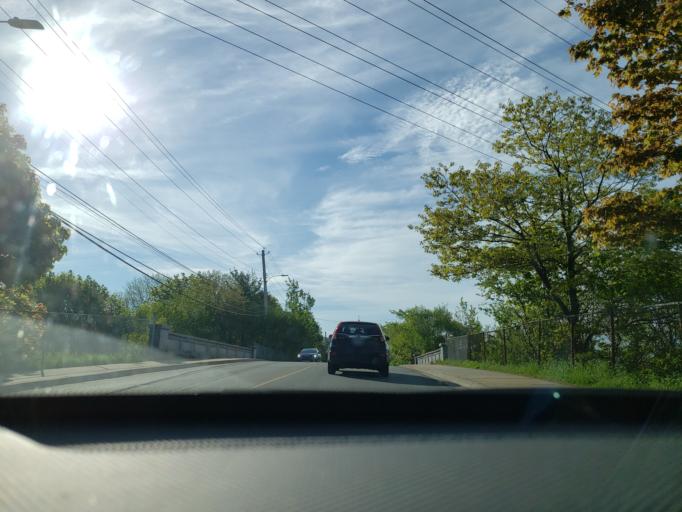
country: CA
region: Nova Scotia
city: Halifax
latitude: 44.6493
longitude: -63.6236
